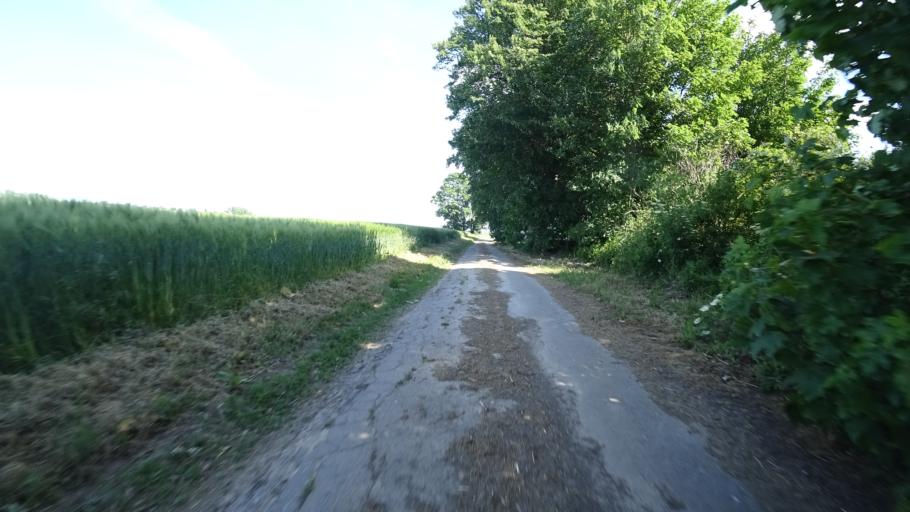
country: DE
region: North Rhine-Westphalia
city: Erwitte
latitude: 51.6173
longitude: 8.3778
